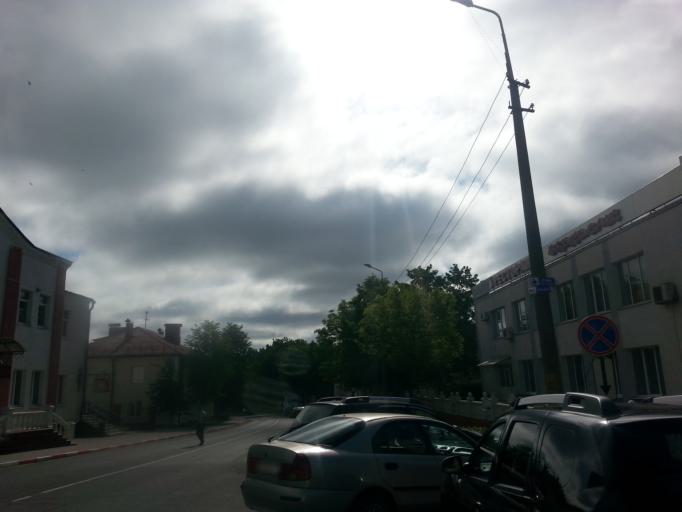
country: BY
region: Vitebsk
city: Hlybokaye
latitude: 55.1388
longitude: 27.6870
